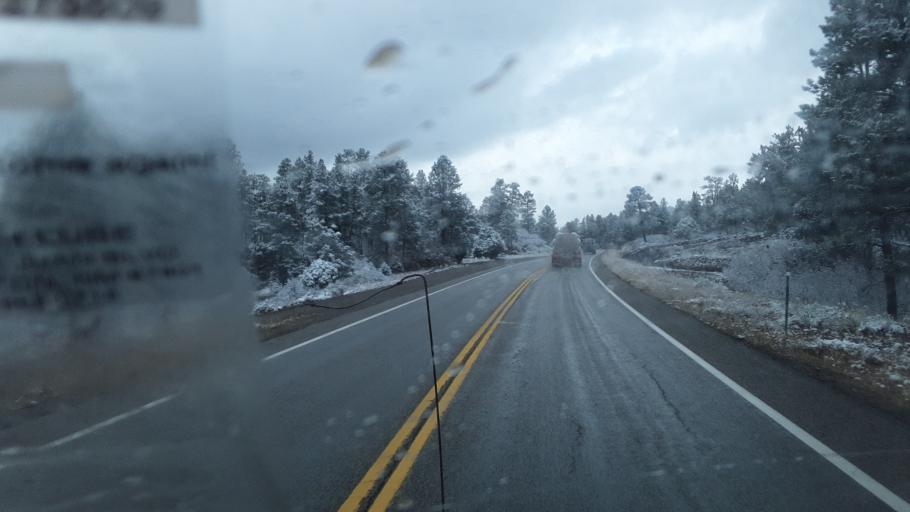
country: US
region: Colorado
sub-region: Archuleta County
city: Pagosa Springs
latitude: 37.2115
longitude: -107.2687
